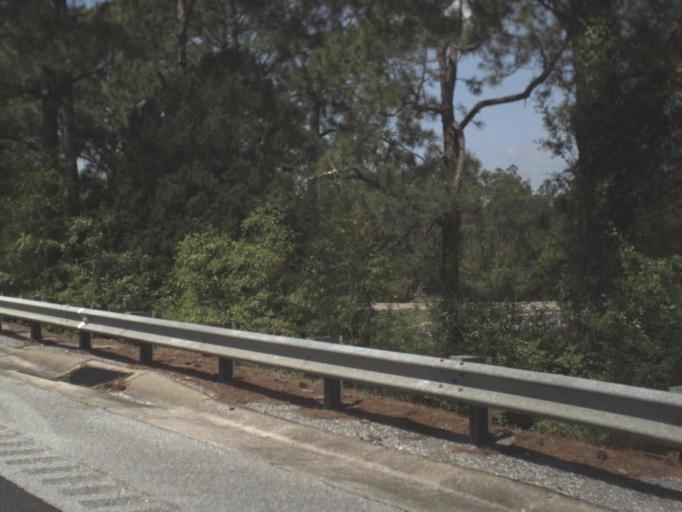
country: US
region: Florida
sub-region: Santa Rosa County
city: Bagdad
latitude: 30.5710
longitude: -87.0303
